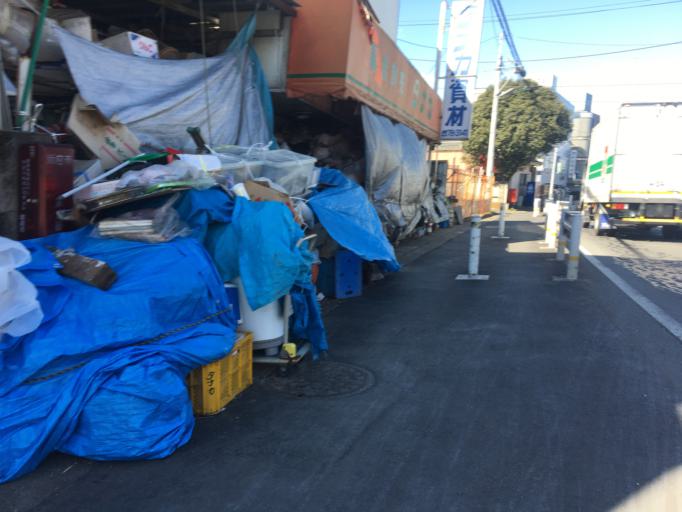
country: JP
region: Saitama
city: Shiki
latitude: 35.8070
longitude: 139.5555
